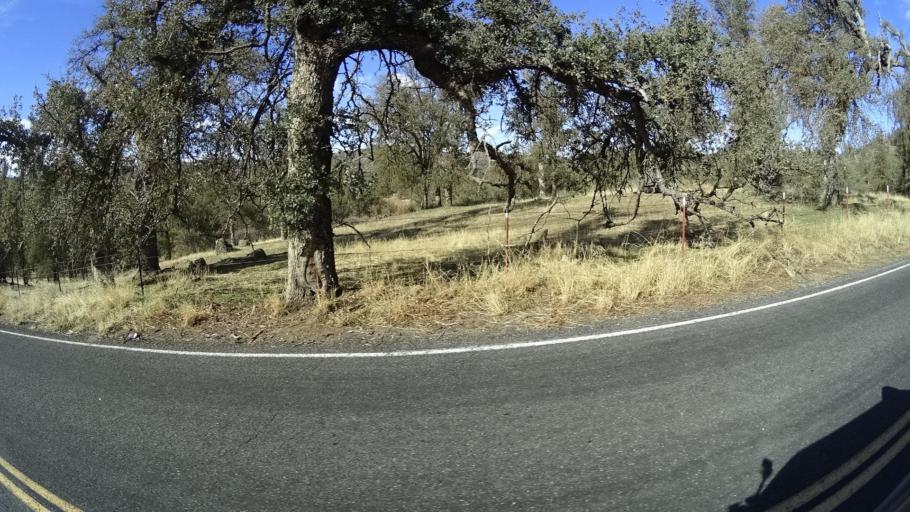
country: US
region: California
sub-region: Kern County
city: Alta Sierra
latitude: 35.7040
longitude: -118.7301
